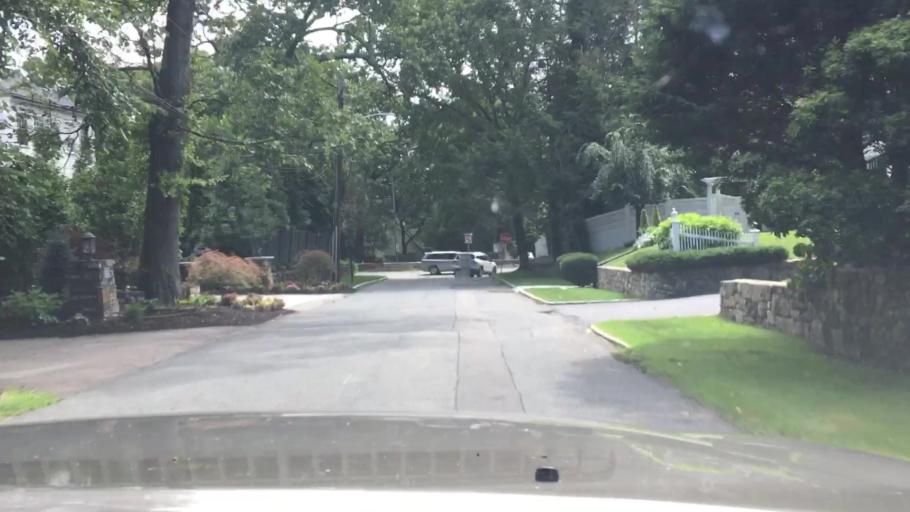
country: US
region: Massachusetts
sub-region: Norfolk County
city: Wellesley
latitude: 42.3108
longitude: -71.2818
